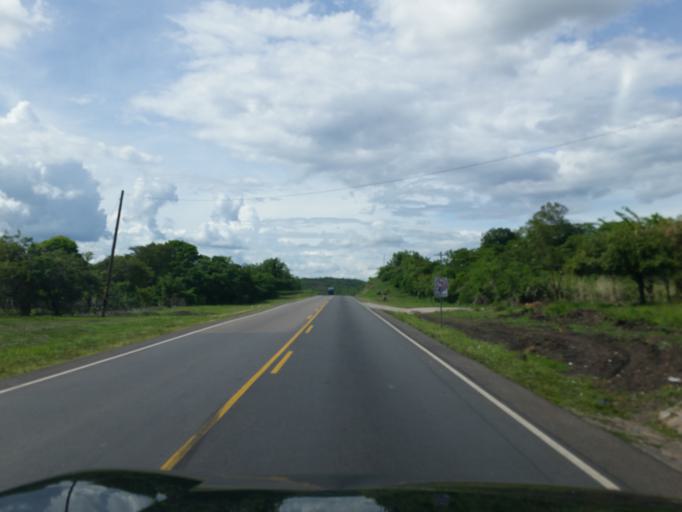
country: NI
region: Matagalpa
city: Ciudad Dario
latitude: 12.5477
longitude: -86.0496
